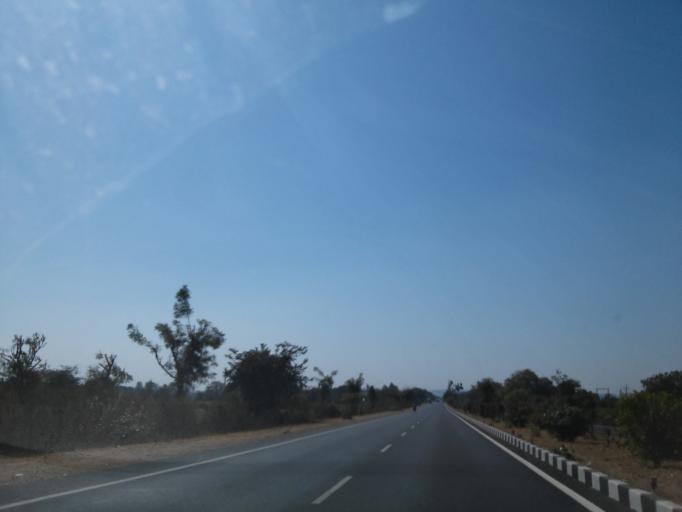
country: IN
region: Gujarat
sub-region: Sabar Kantha
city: Modasa
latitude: 23.6341
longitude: 73.3028
